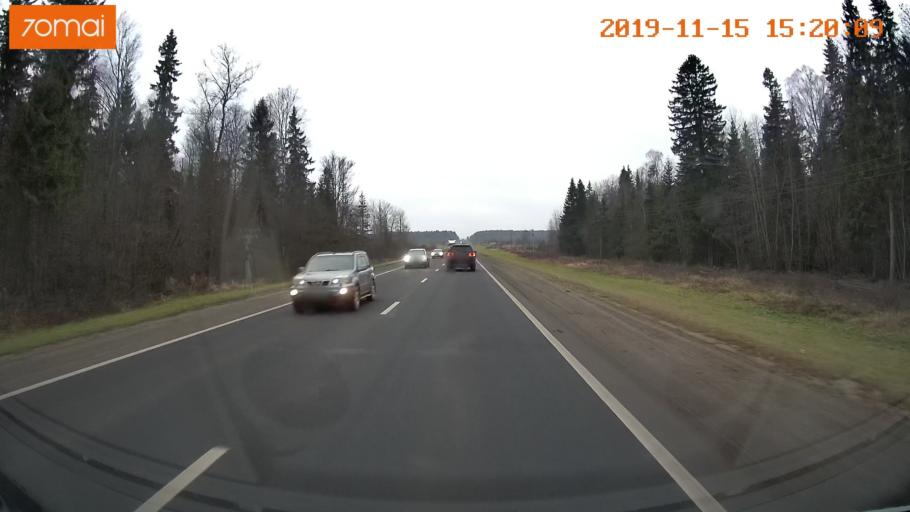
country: RU
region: Jaroslavl
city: Danilov
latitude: 58.2267
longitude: 40.1664
